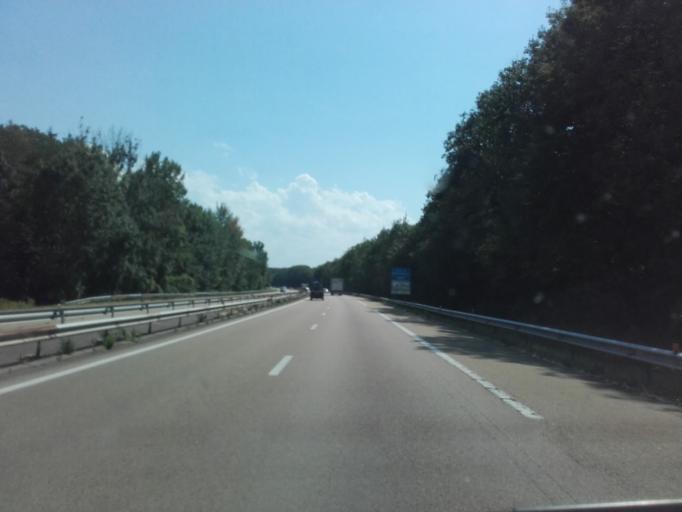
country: FR
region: Bourgogne
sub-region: Departement de l'Yonne
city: Joux-la-Ville
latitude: 47.6032
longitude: 3.9095
